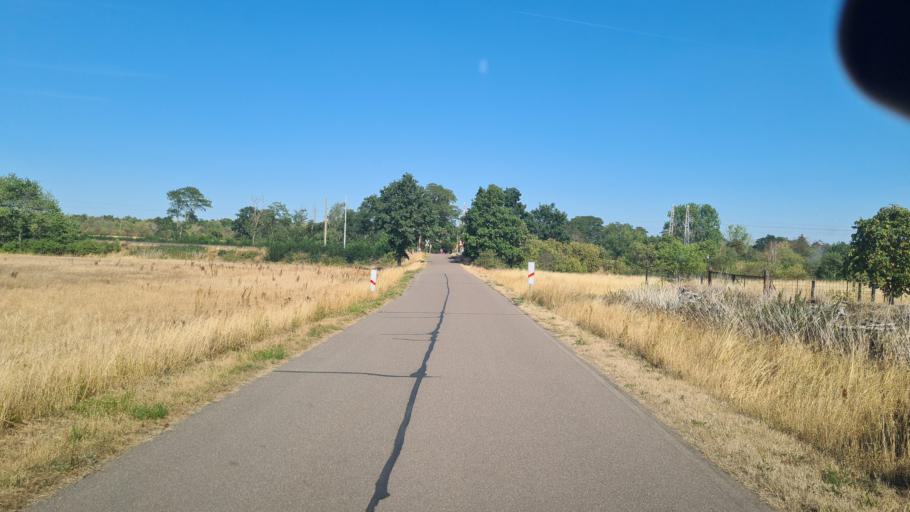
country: DE
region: Saxony
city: Zeithain
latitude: 51.3818
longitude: 13.3106
